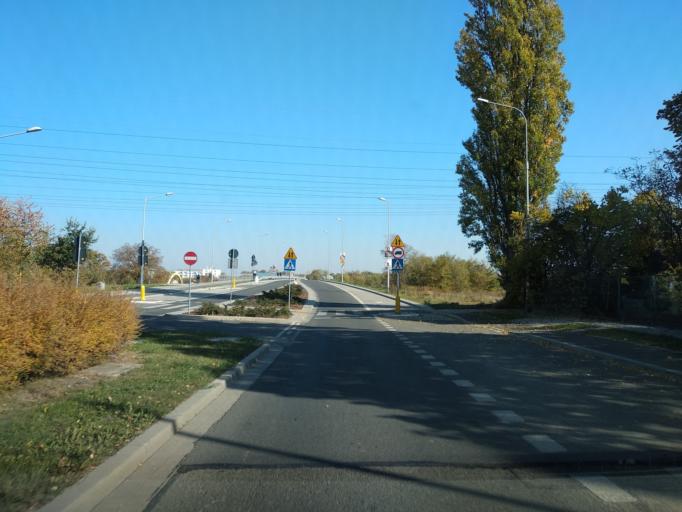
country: PL
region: Lower Silesian Voivodeship
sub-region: Powiat wroclawski
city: Bielany Wroclawskie
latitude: 51.0768
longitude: 16.9800
